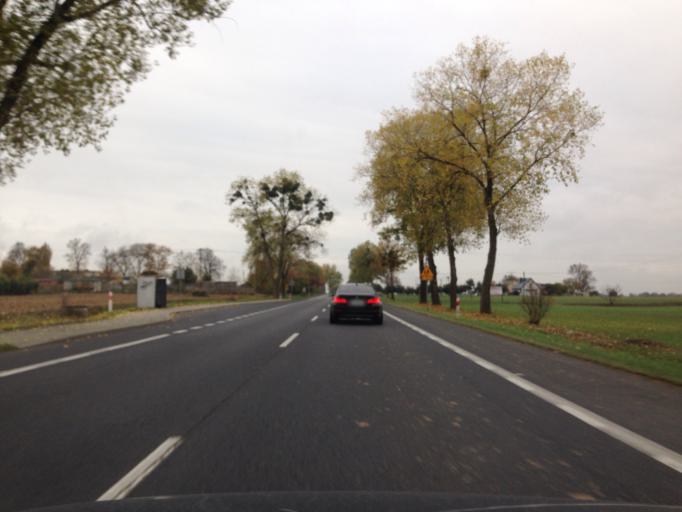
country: PL
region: Kujawsko-Pomorskie
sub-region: Powiat swiecki
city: Pruszcz
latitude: 53.3207
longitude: 18.2780
